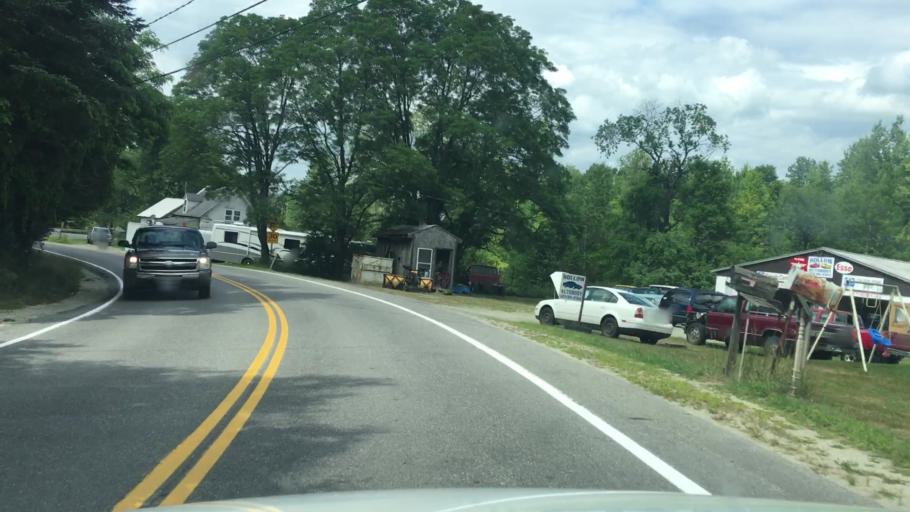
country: US
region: New Hampshire
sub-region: Grafton County
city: Deerfield
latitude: 44.2927
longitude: -71.6564
